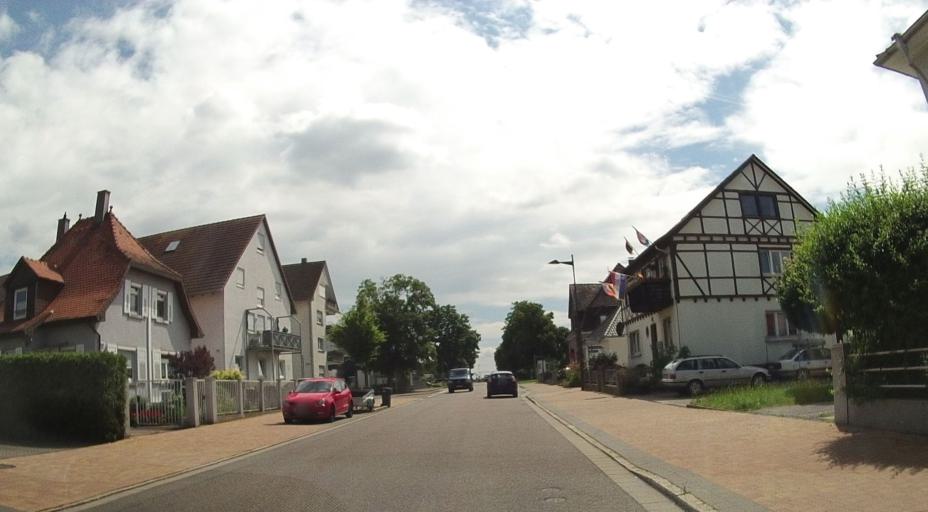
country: DE
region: Baden-Wuerttemberg
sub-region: Karlsruhe Region
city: Durmersheim
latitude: 48.9255
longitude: 8.2648
